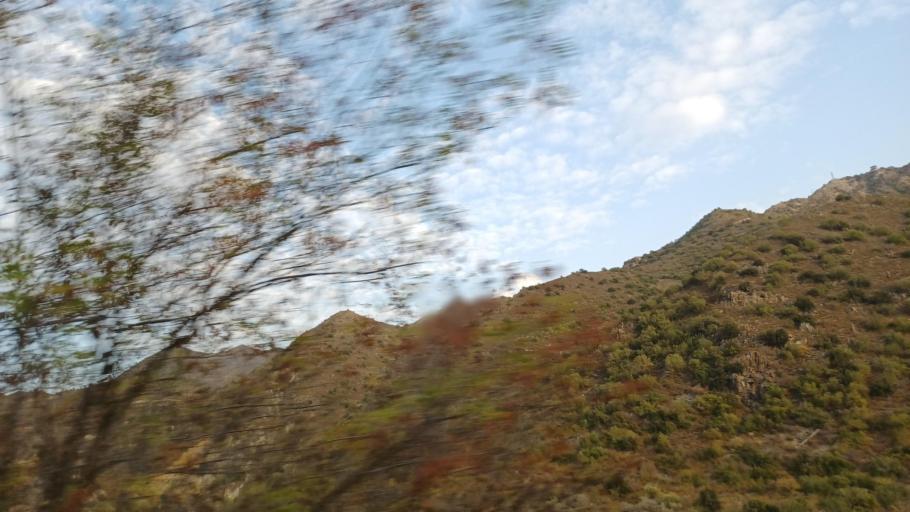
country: CY
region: Limassol
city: Pelendri
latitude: 34.8885
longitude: 32.9325
